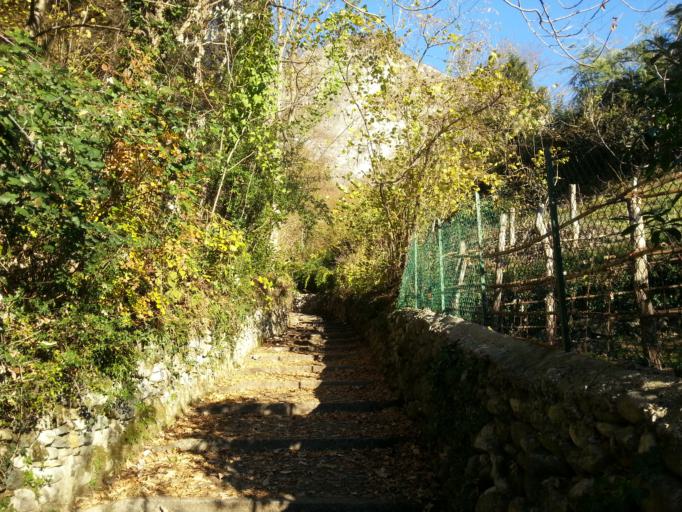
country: IT
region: Lombardy
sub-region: Provincia di Como
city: Griante
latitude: 46.0003
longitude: 9.2294
